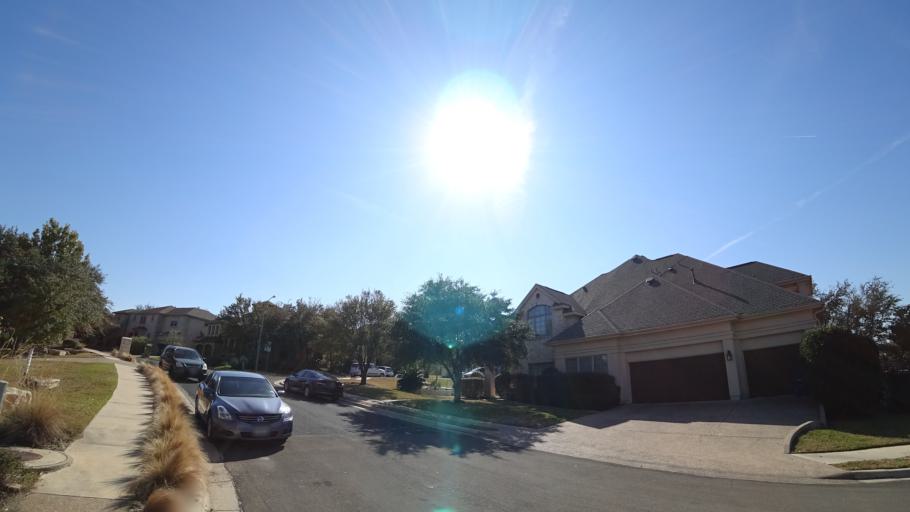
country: US
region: Texas
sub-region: Williamson County
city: Jollyville
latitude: 30.3728
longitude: -97.7672
